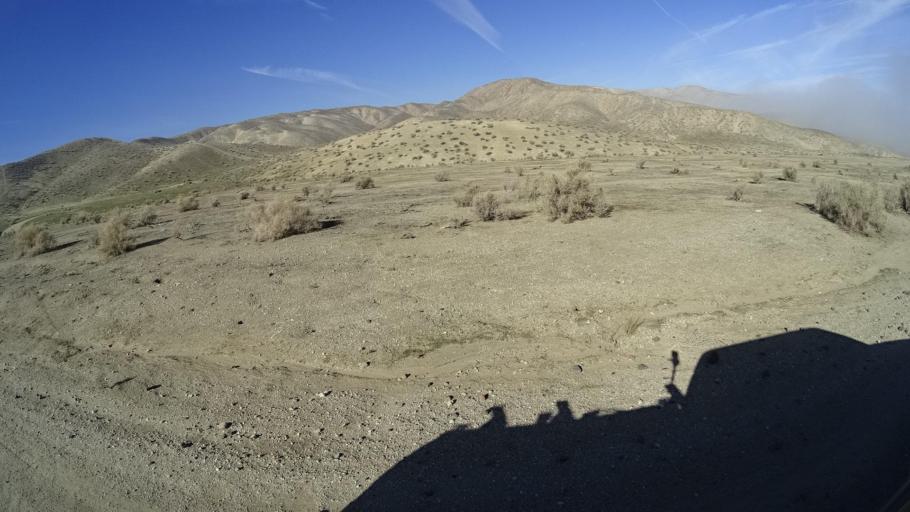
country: US
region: California
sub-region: Kern County
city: Maricopa
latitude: 35.0132
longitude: -119.4542
